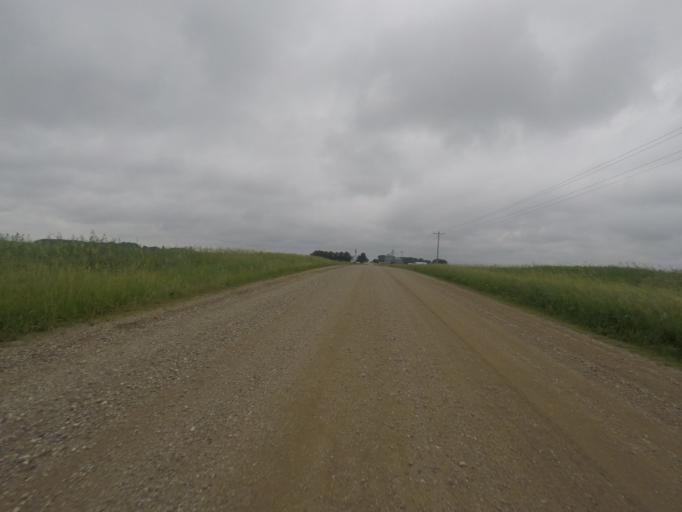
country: US
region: Minnesota
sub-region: Steele County
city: Owatonna
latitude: 44.0373
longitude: -93.1019
